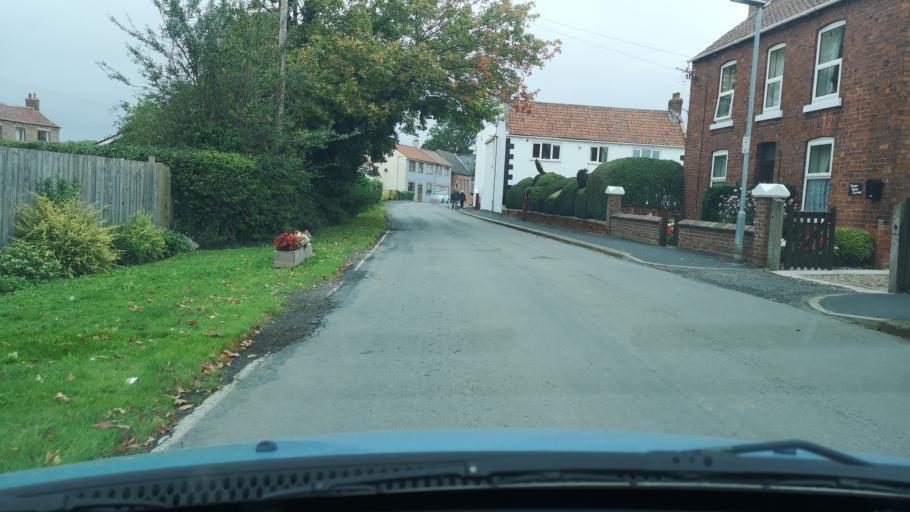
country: GB
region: England
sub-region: North Lincolnshire
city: Burton upon Stather
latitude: 53.6610
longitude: -0.7181
